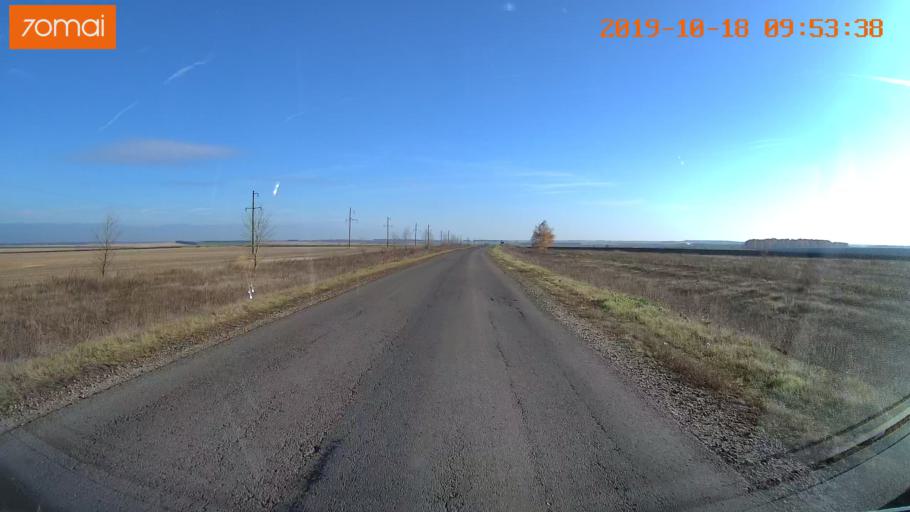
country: RU
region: Tula
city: Kazachka
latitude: 53.3625
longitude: 38.3332
